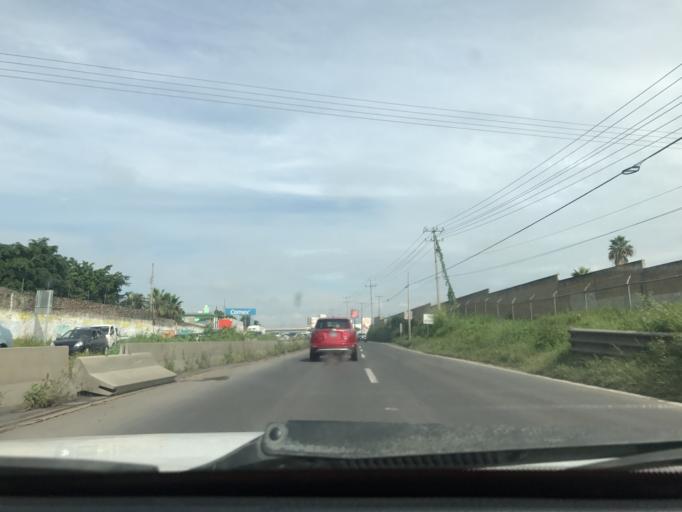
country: MX
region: Morelos
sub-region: Cuautla
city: Tierra Larga (Campo Nuevo)
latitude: 18.8478
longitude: -98.9326
